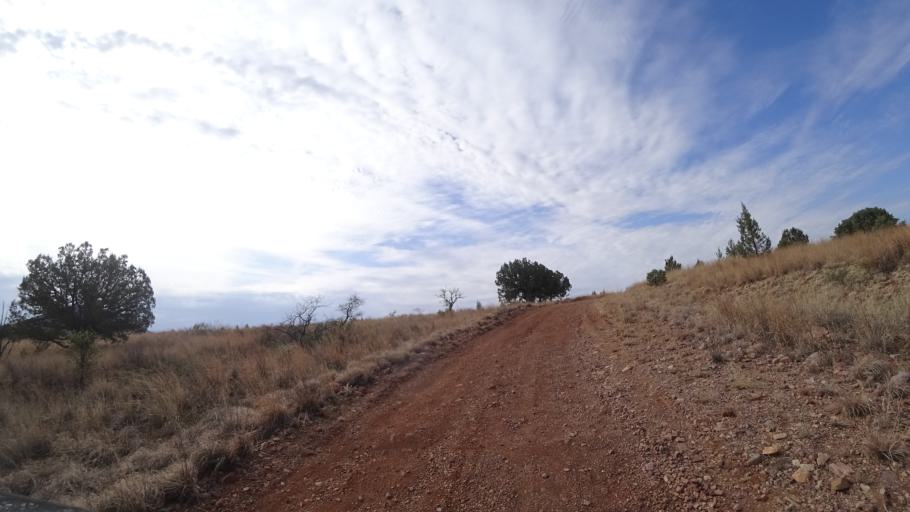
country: MX
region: Sonora
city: Santa Cruz
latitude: 31.4832
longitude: -110.5688
